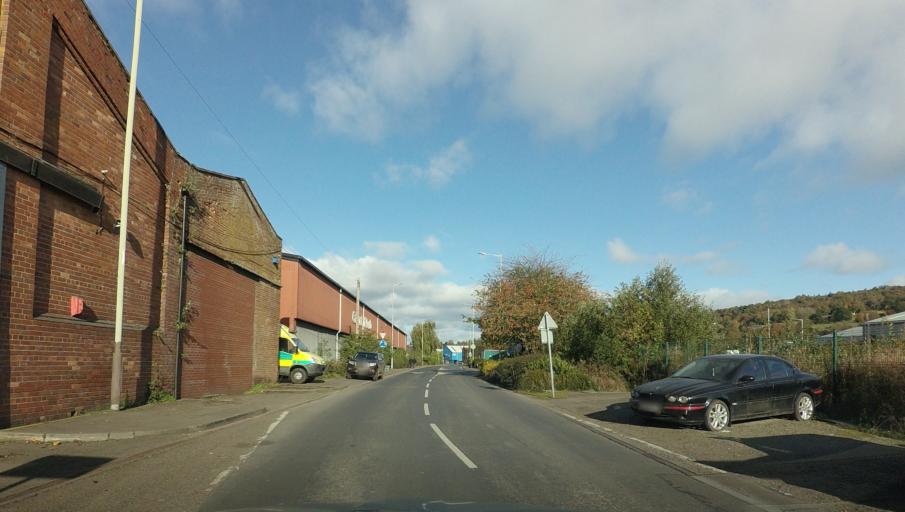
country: GB
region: Scotland
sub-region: Perth and Kinross
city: Perth
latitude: 56.3825
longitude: -3.4285
